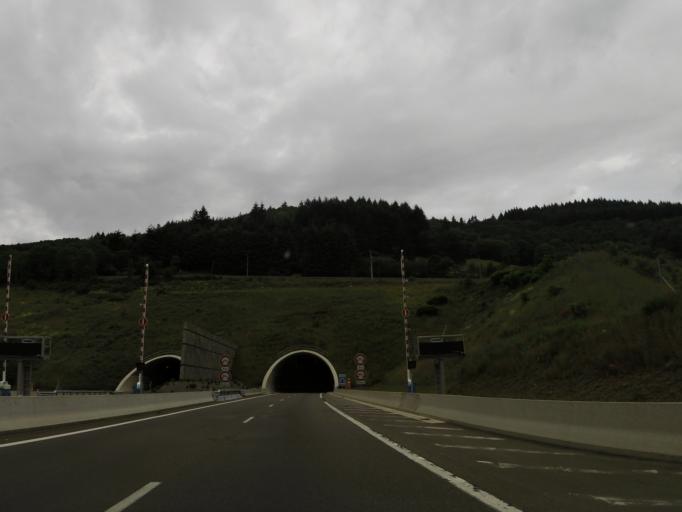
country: FR
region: Rhone-Alpes
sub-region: Departement du Rhone
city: Tarare
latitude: 45.8820
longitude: 4.4300
